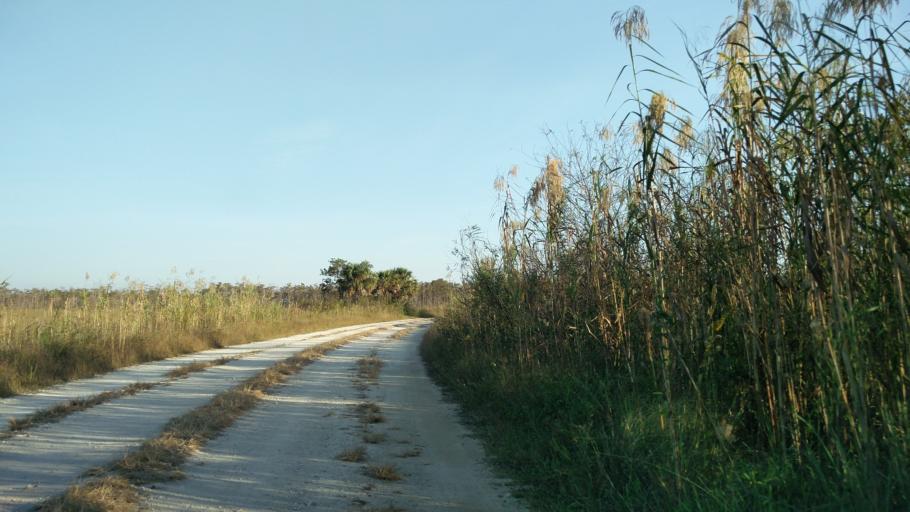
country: US
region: Florida
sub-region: Collier County
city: Lely Resort
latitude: 25.9795
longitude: -81.3718
